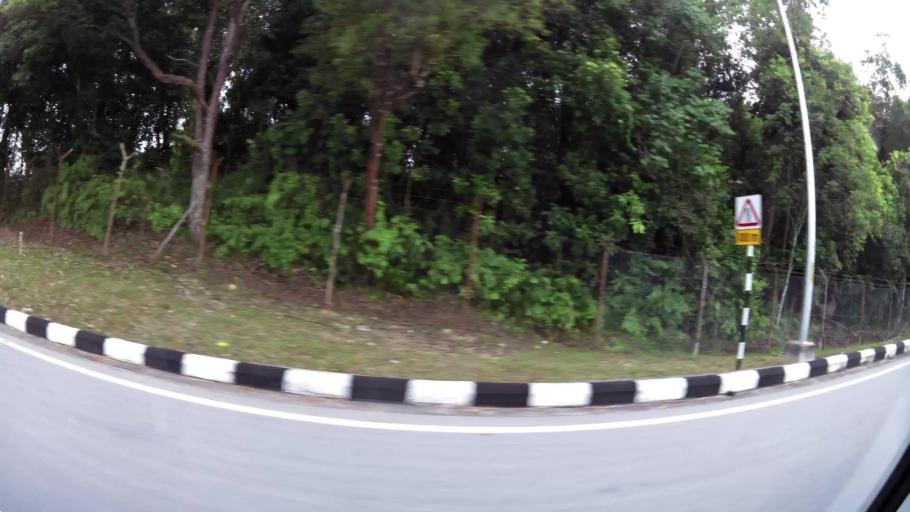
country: BN
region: Brunei and Muara
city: Bandar Seri Begawan
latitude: 4.9136
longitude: 114.9031
